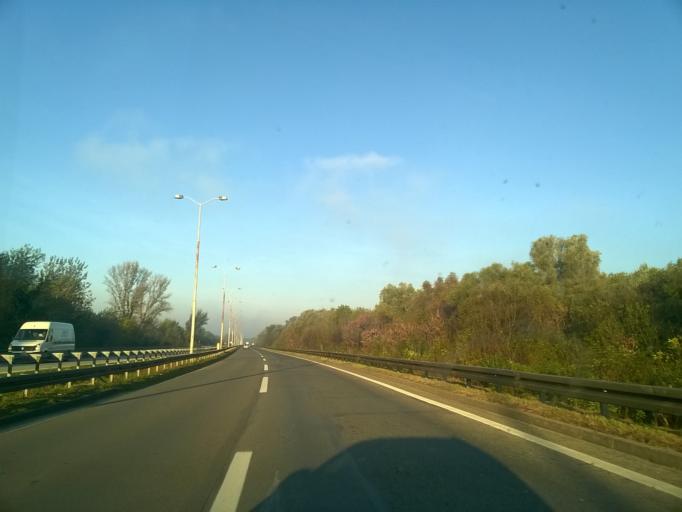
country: RS
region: Autonomna Pokrajina Vojvodina
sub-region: Juznobanatski Okrug
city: Pancevo
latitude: 44.8573
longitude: 20.6223
